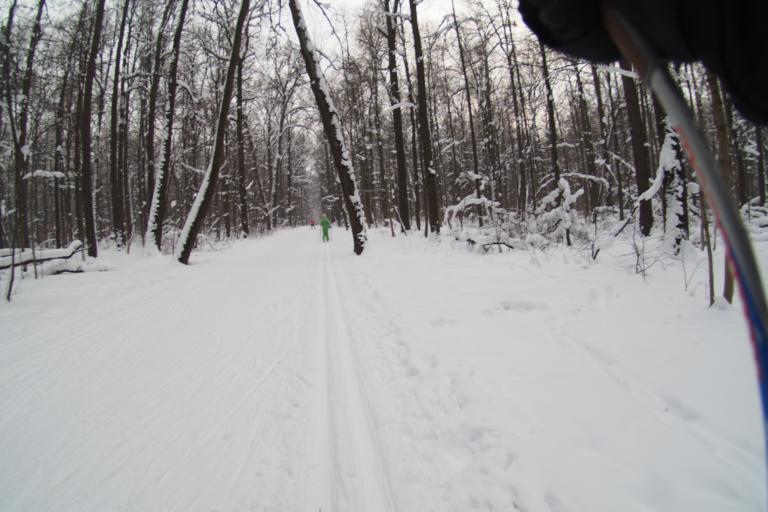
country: RU
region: Moskovskaya
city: Izmaylovo
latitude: 55.7710
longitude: 37.7772
